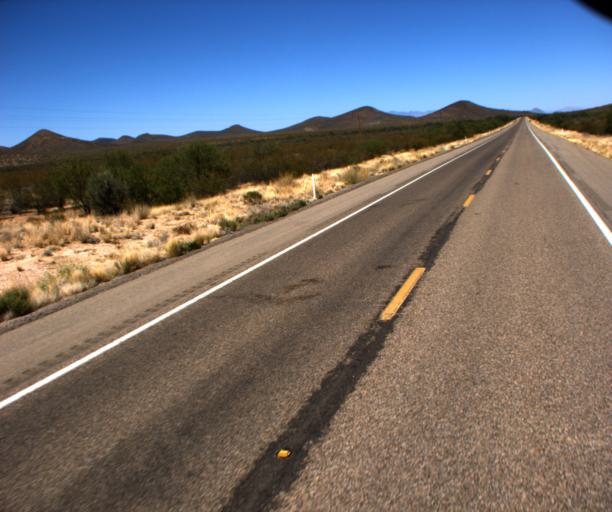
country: US
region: Arizona
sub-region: Pima County
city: Three Points
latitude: 32.0536
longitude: -111.4122
